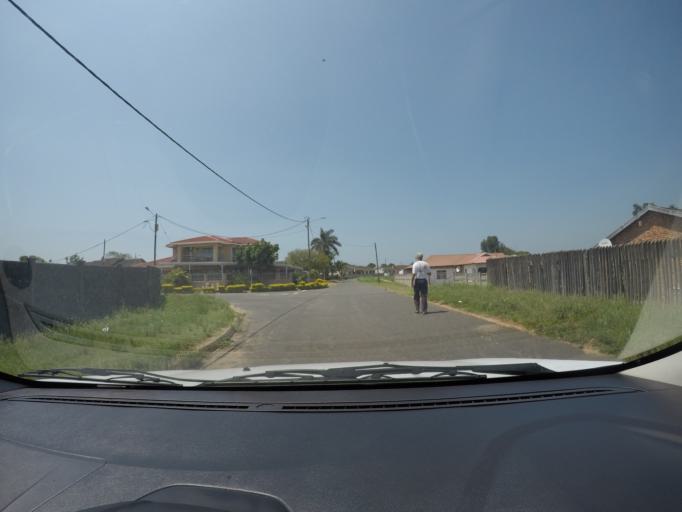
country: ZA
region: KwaZulu-Natal
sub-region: uThungulu District Municipality
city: eSikhawini
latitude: -28.8660
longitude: 31.9228
